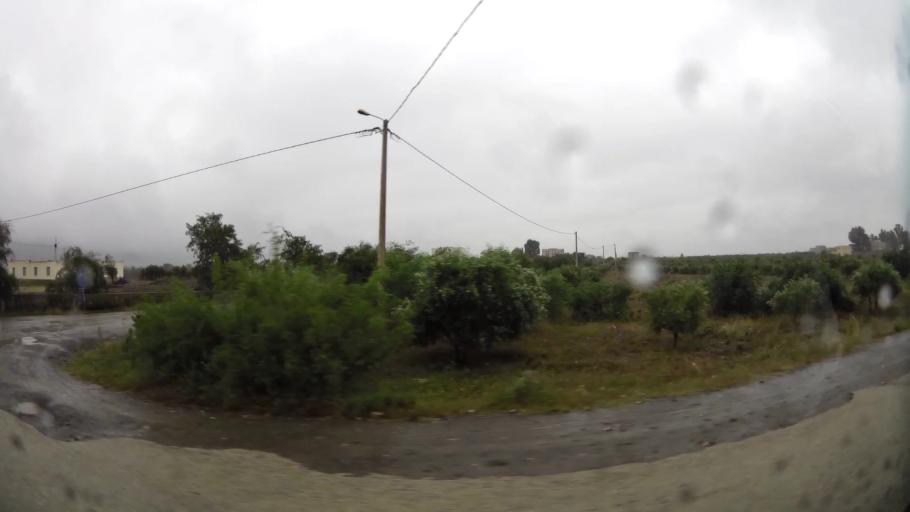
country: MA
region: Taza-Al Hoceima-Taounate
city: Imzourene
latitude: 35.1419
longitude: -3.7964
